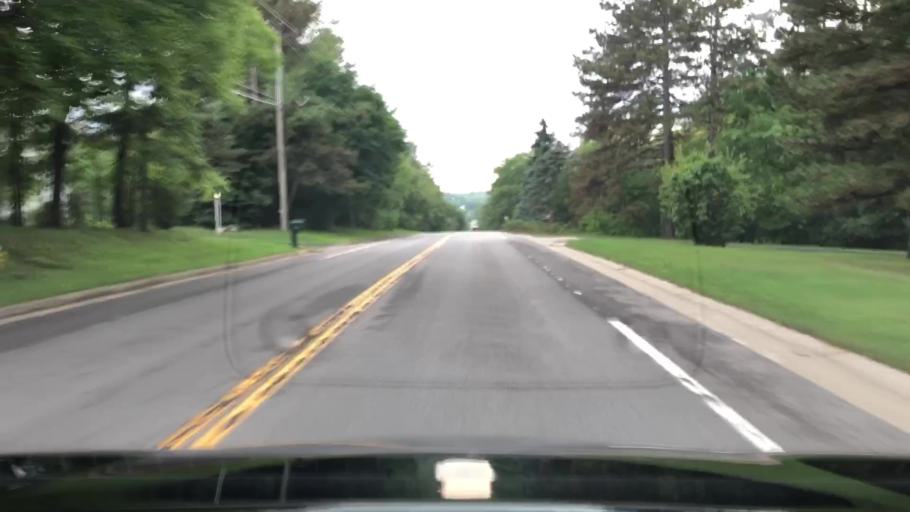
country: US
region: New York
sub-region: Erie County
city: Orchard Park
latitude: 42.7522
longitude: -78.7084
